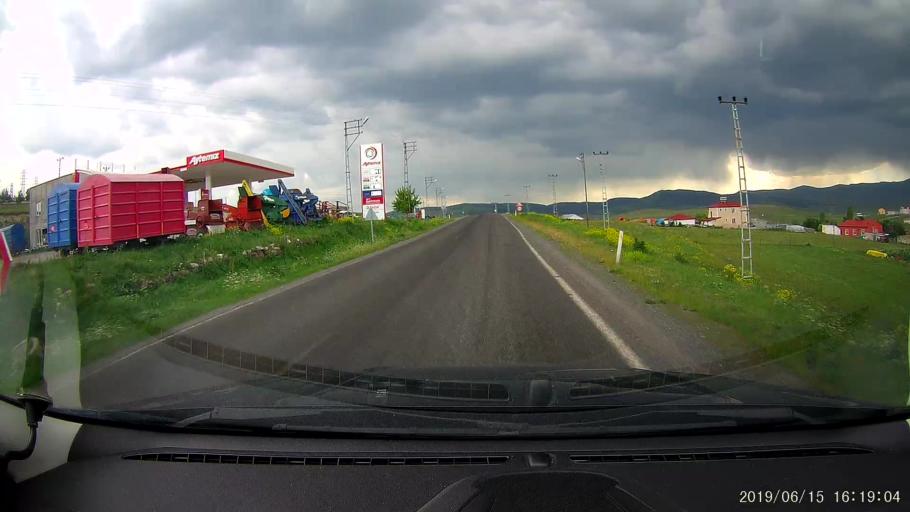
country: TR
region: Ardahan
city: Hanak
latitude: 41.2324
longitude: 42.8523
